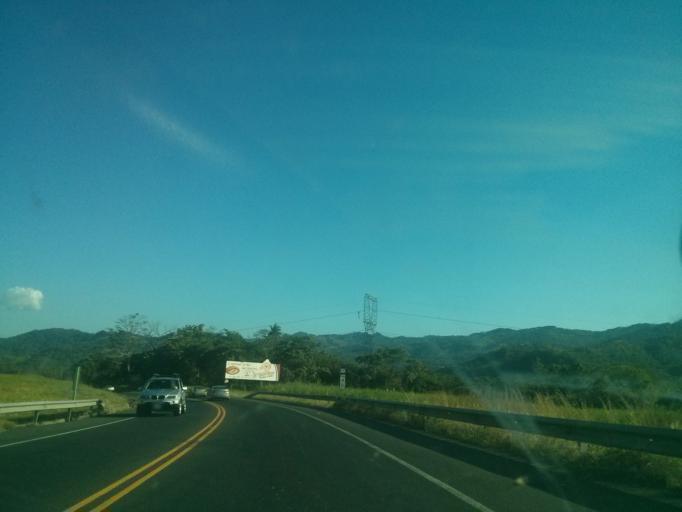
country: CR
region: Alajuela
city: Atenas
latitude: 9.9325
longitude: -84.4183
